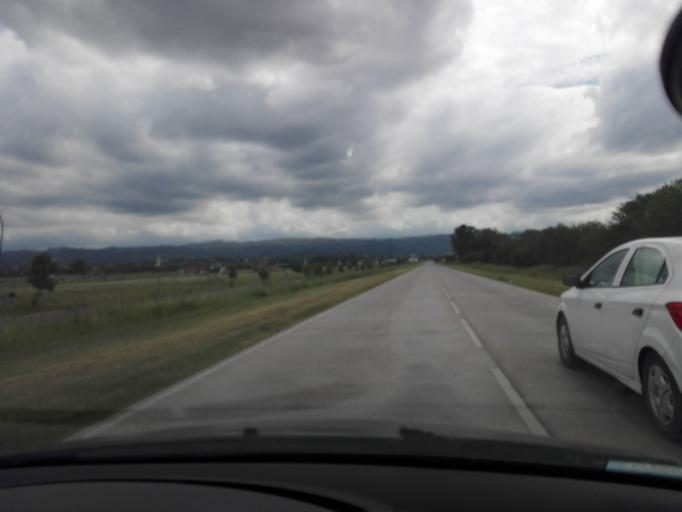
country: AR
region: Cordoba
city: Alta Gracia
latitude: -31.6347
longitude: -64.4182
